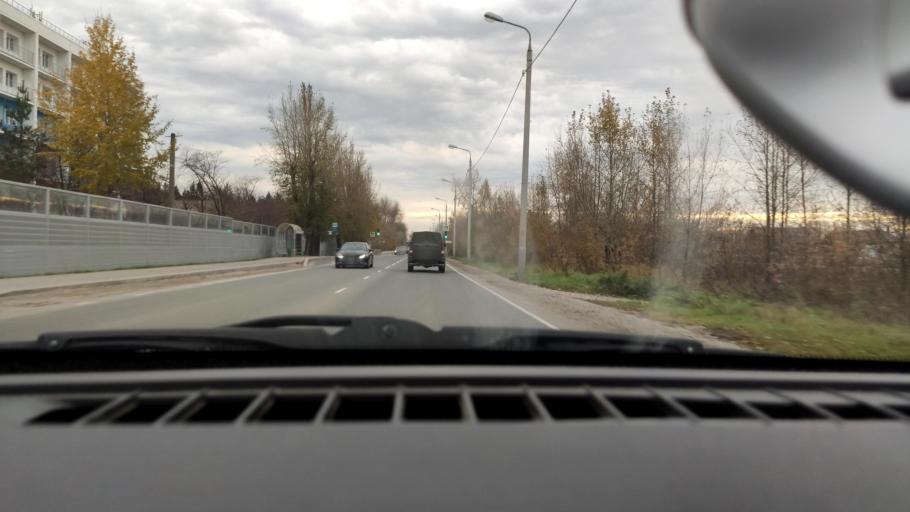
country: RU
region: Perm
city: Kondratovo
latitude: 57.9784
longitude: 56.1303
